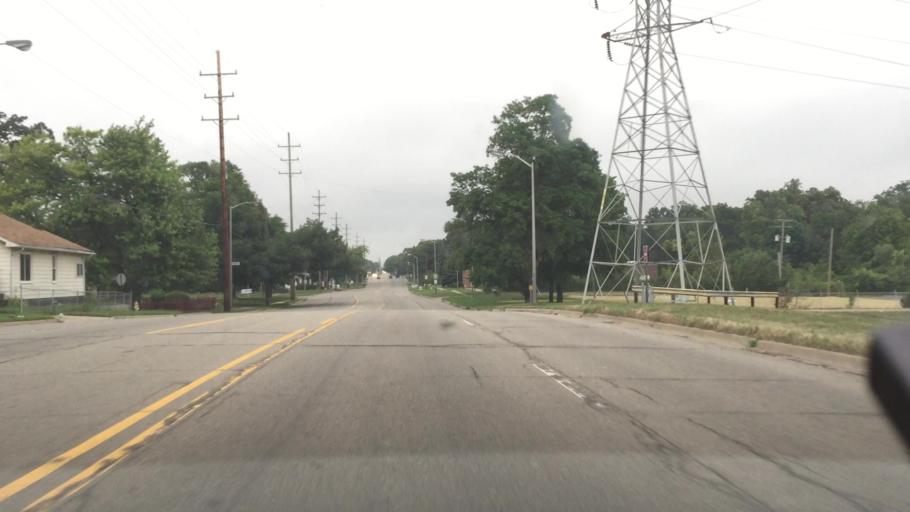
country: US
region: Michigan
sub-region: Oakland County
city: Pontiac
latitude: 42.6231
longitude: -83.2684
